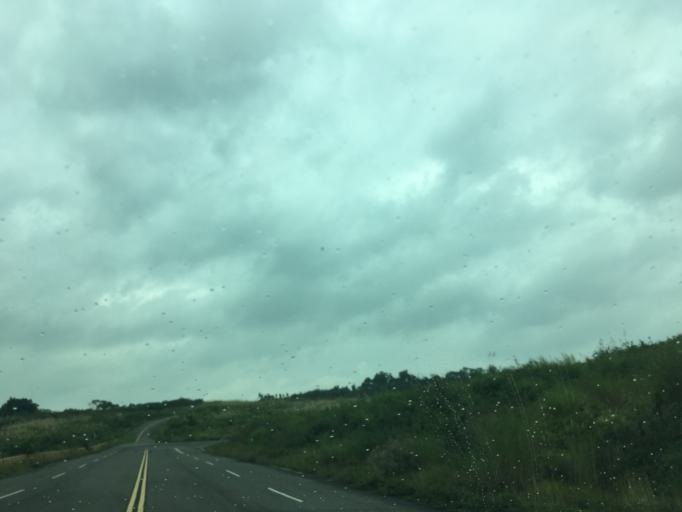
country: TW
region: Taiwan
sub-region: Taichung City
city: Taichung
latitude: 24.0574
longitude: 120.7296
